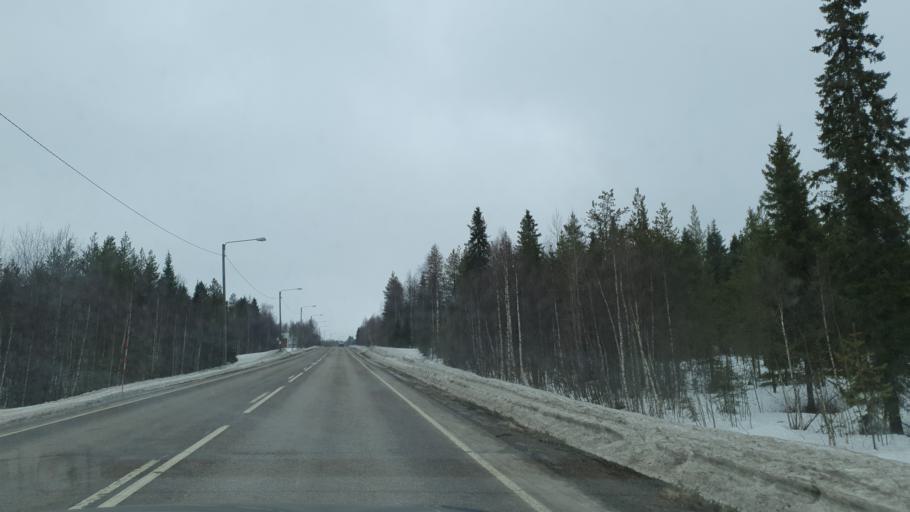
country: FI
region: Lapland
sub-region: Torniolaakso
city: Pello
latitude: 66.8824
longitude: 24.0708
